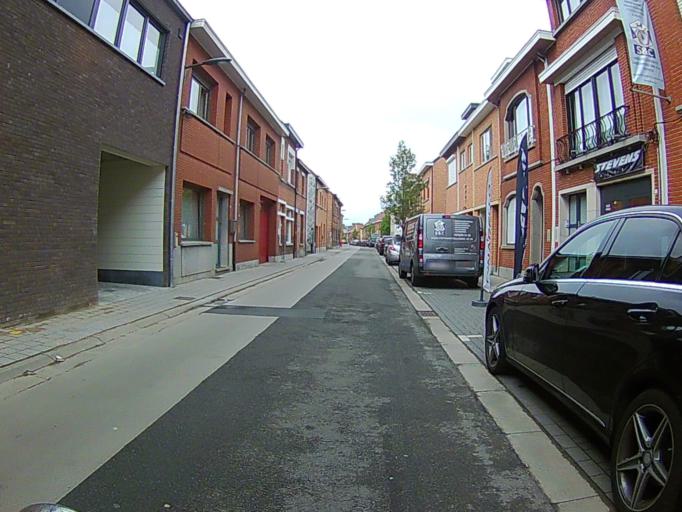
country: BE
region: Flanders
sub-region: Provincie Antwerpen
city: Bornem
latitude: 51.0961
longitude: 4.2405
